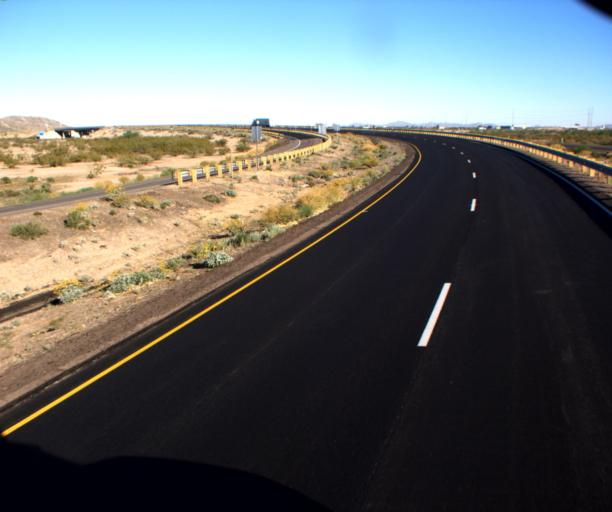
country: US
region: Arizona
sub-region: Pinal County
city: Arizona City
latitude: 32.8174
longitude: -111.6791
